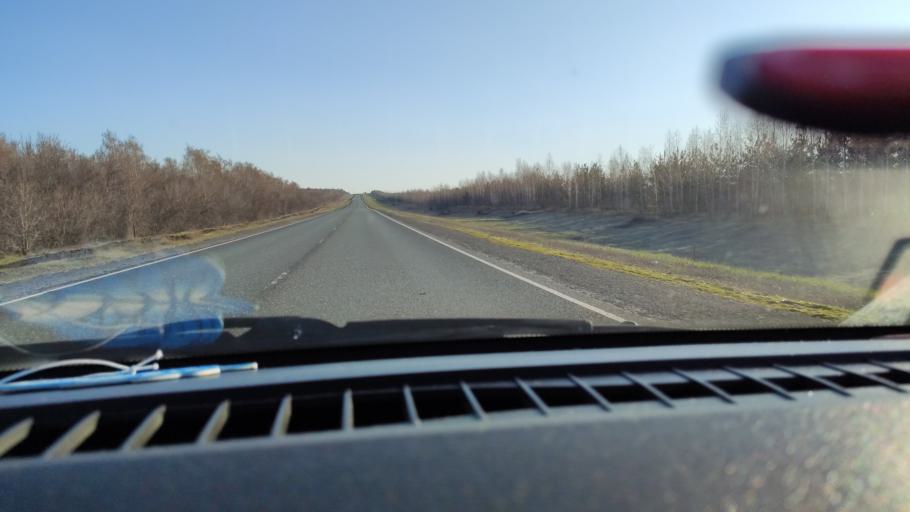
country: RU
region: Saratov
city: Balakovo
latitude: 52.1488
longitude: 47.8094
